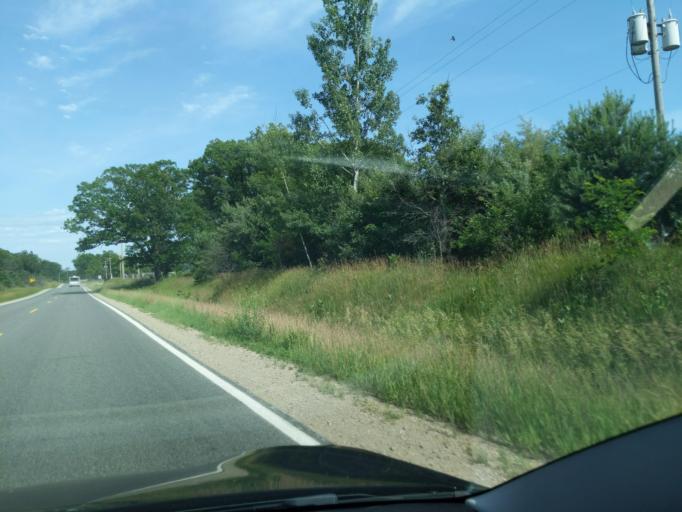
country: US
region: Michigan
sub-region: Muskegon County
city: Whitehall
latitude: 43.4098
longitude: -86.3026
